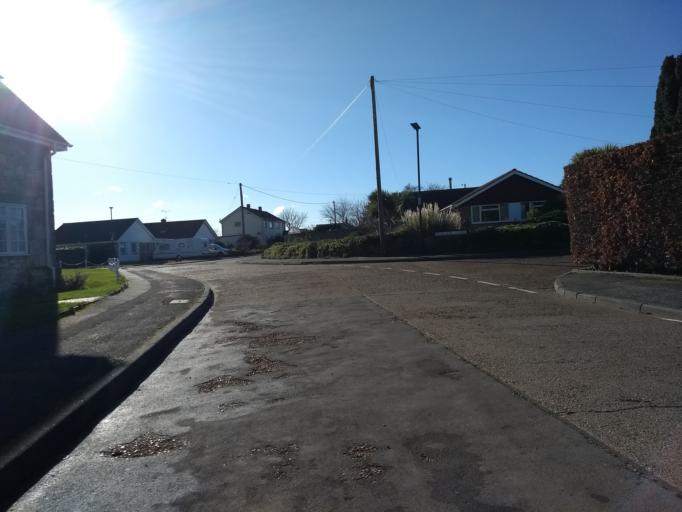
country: GB
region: England
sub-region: Isle of Wight
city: Bembridge
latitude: 50.6849
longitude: -1.0738
